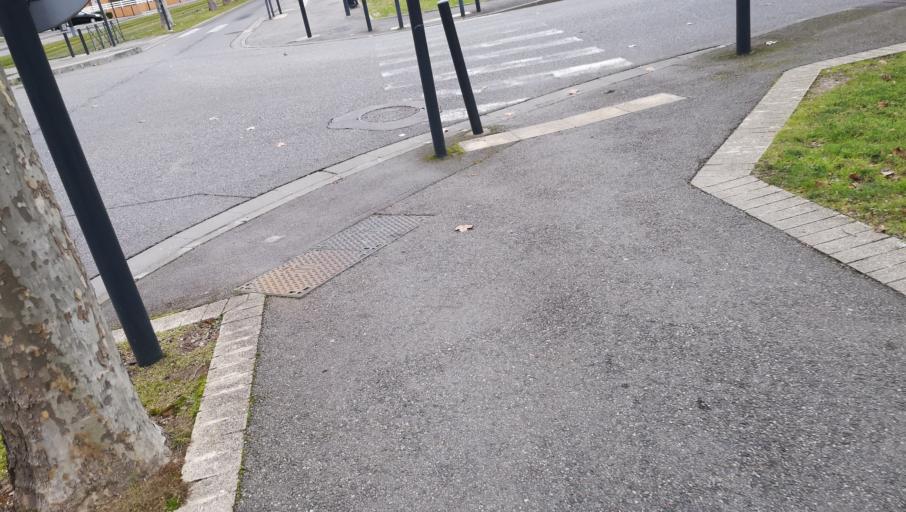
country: FR
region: Midi-Pyrenees
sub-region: Departement de la Haute-Garonne
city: Blagnac
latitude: 43.6361
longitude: 1.3857
